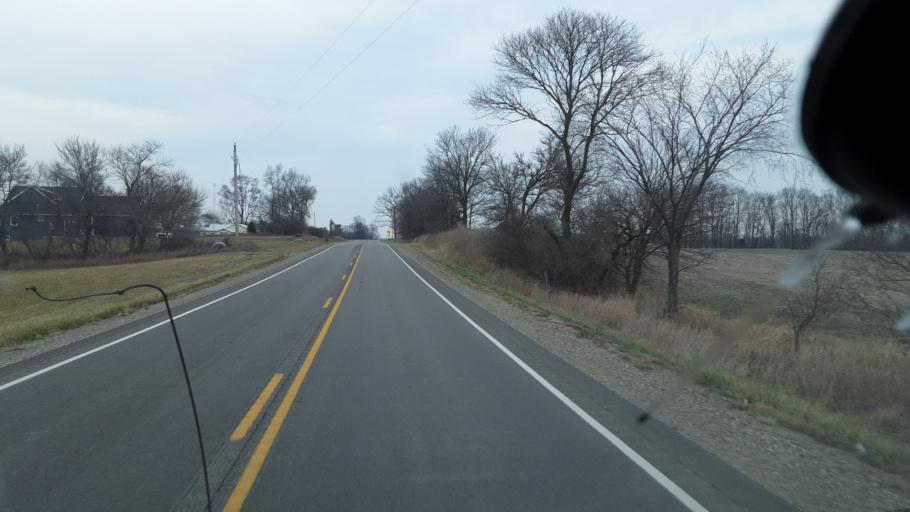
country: US
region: Indiana
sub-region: Steuben County
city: Angola
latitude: 41.6210
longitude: -85.1698
